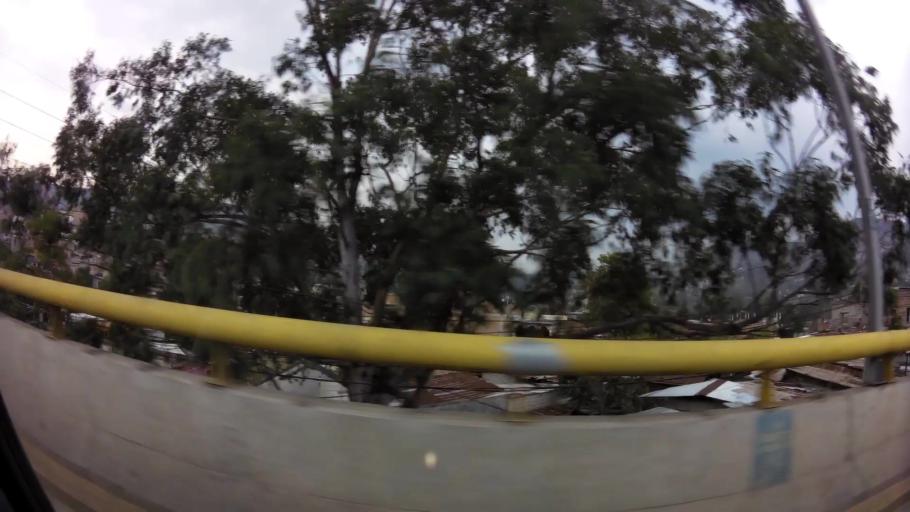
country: HN
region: Francisco Morazan
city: El Lolo
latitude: 14.1032
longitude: -87.2378
